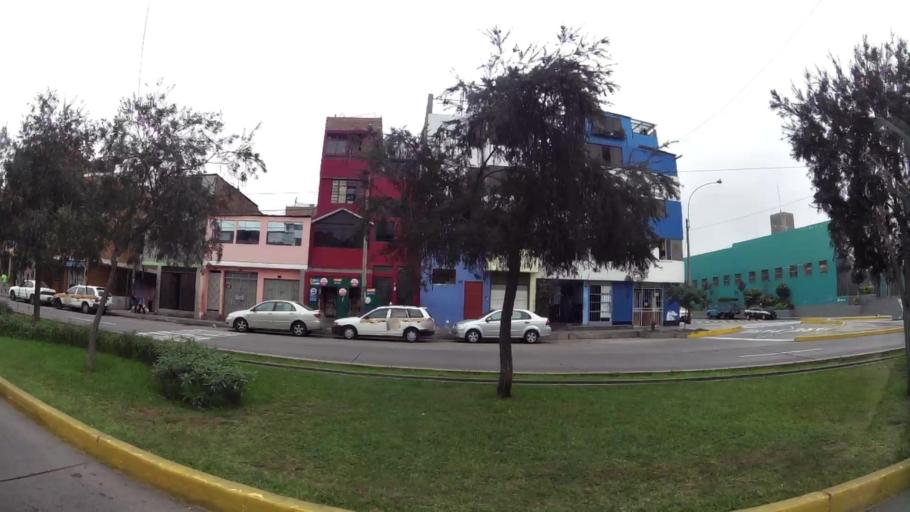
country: PE
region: Lima
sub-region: Lima
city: Surco
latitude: -12.1087
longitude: -77.0081
